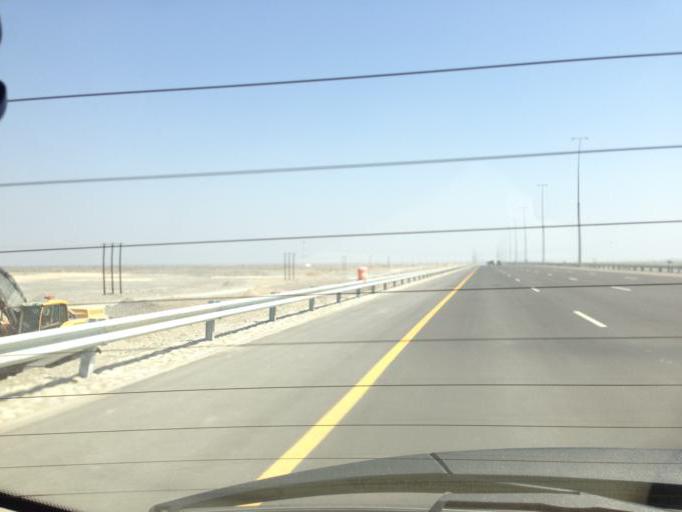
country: OM
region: Al Batinah
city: Barka'
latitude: 23.5478
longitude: 57.6837
